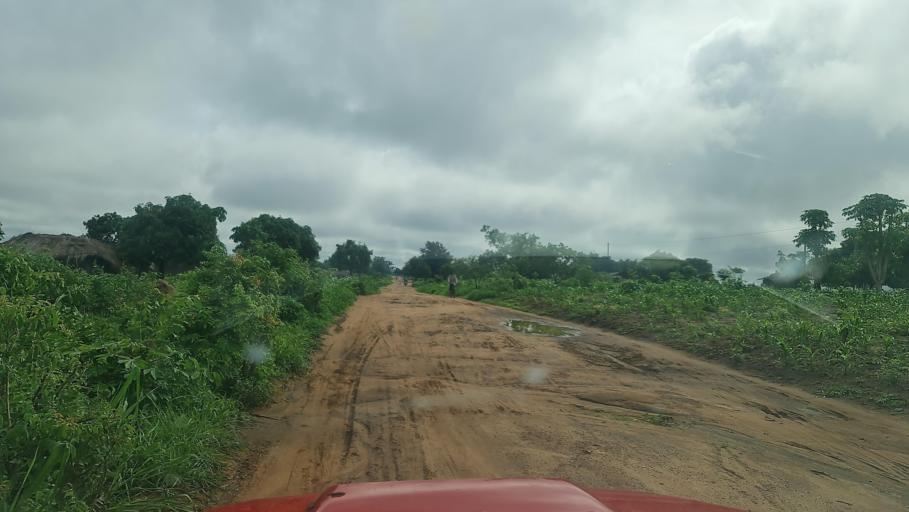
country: MW
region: Southern Region
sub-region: Nsanje District
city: Nsanje
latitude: -17.2219
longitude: 35.6679
